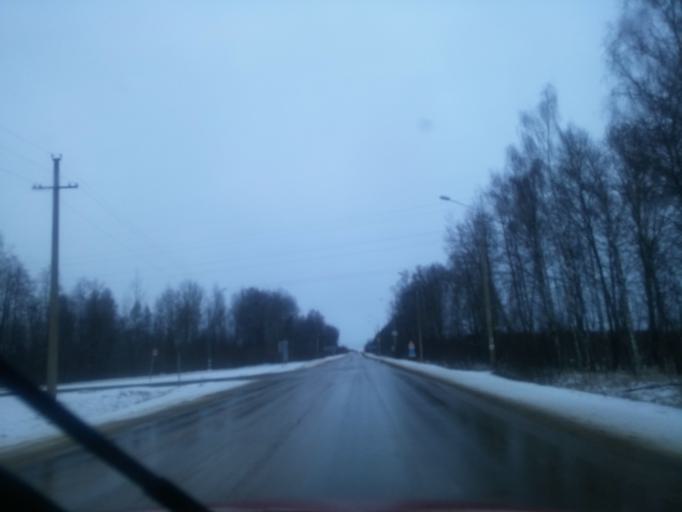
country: RU
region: Tverskaya
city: Likhoslavl'
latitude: 56.9546
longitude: 35.4279
